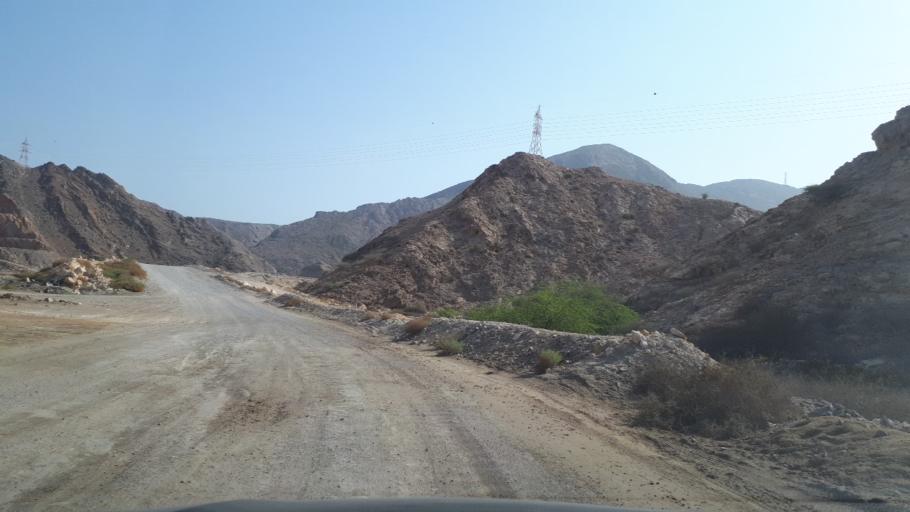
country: OM
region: Muhafazat Masqat
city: Muscat
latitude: 23.5371
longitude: 58.6519
